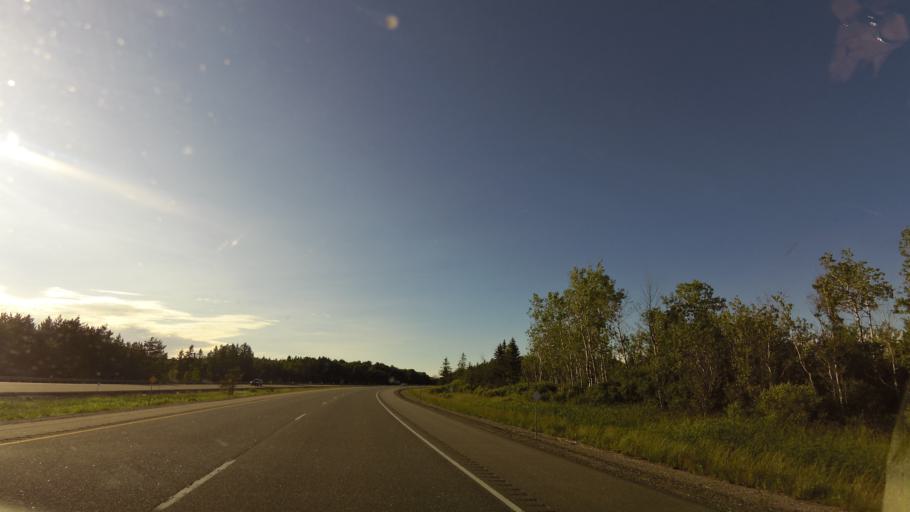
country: CA
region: Ontario
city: Barrie
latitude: 44.5282
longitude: -79.7445
